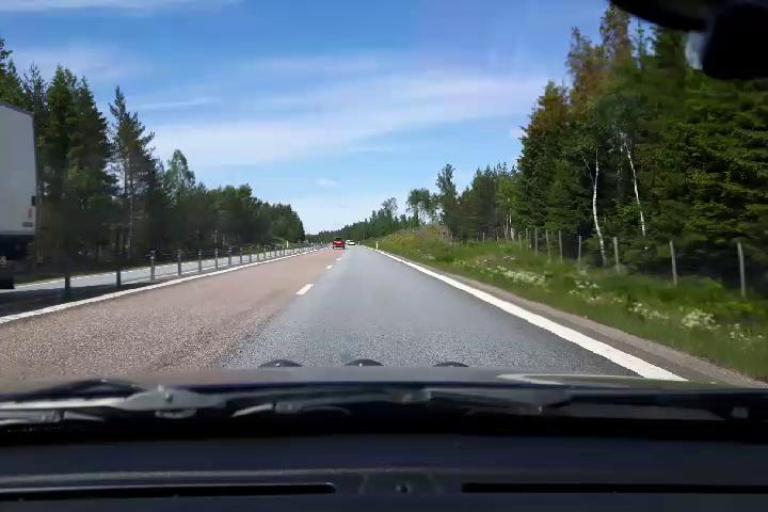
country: SE
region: Gaevleborg
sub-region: Gavle Kommun
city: Norrsundet
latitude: 60.8176
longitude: 17.0843
